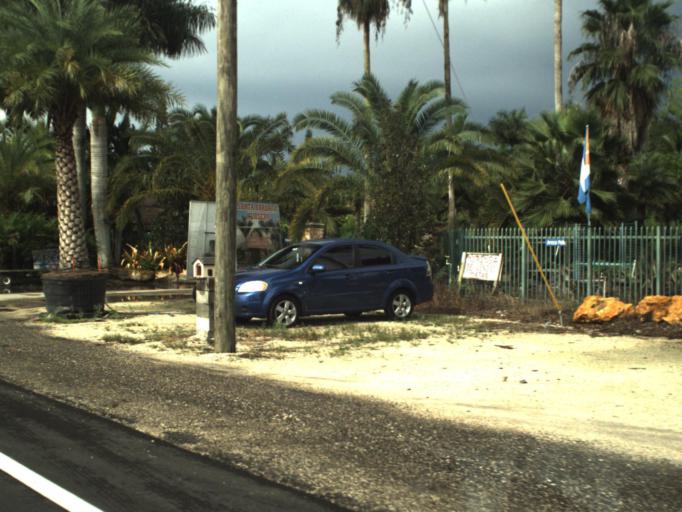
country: US
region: Florida
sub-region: Miami-Dade County
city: Richmond West
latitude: 25.5753
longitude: -80.4783
